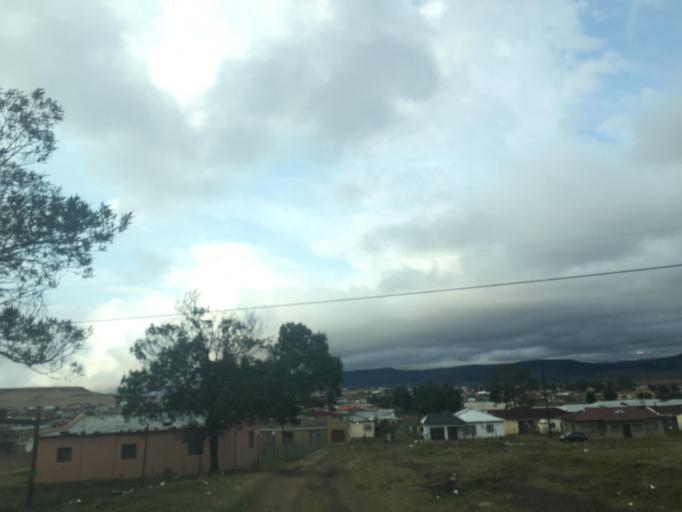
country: ZA
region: Eastern Cape
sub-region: Chris Hani District Municipality
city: Cala
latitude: -31.5285
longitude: 27.6983
